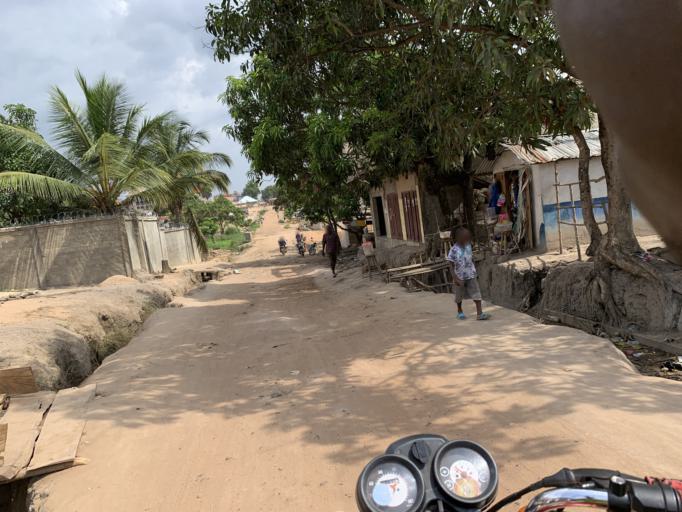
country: SL
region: Western Area
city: Waterloo
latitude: 8.3334
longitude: -13.0527
